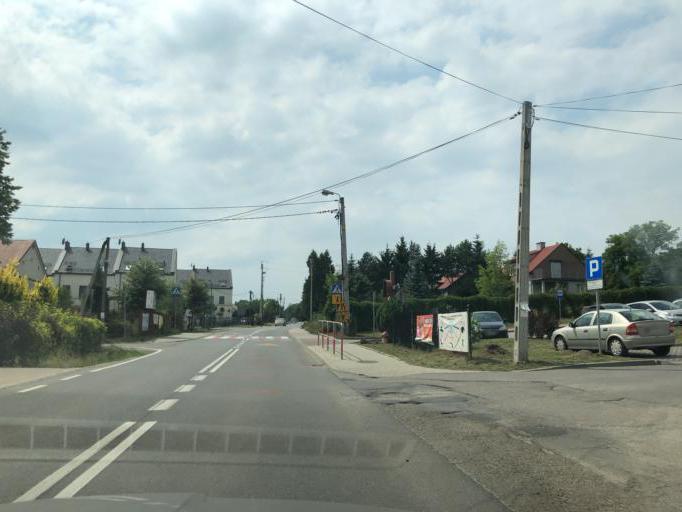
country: PL
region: Lesser Poland Voivodeship
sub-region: Powiat wielicki
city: Wieliczka
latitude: 49.9898
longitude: 20.0332
